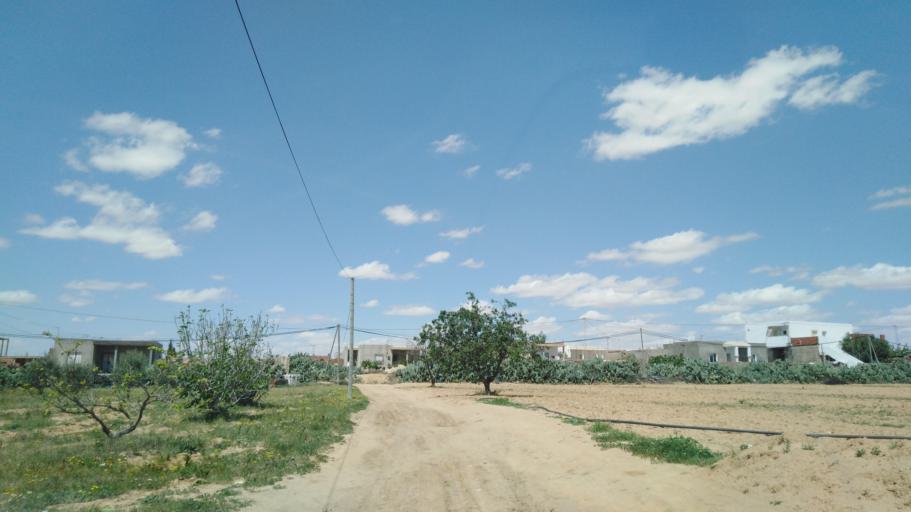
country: TN
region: Safaqis
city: Sfax
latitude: 34.7479
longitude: 10.5390
